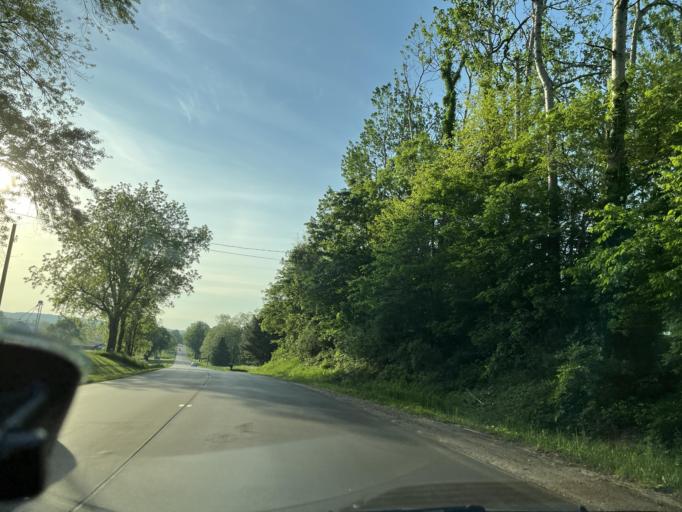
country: US
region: Michigan
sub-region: Barry County
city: Middleville
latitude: 42.7111
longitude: -85.4420
